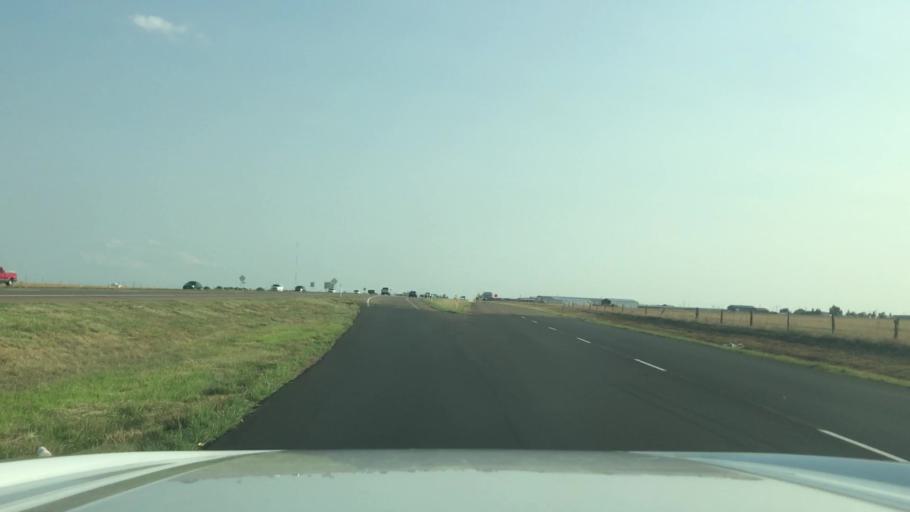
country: US
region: Texas
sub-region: Randall County
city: Canyon
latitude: 35.0998
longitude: -101.9137
